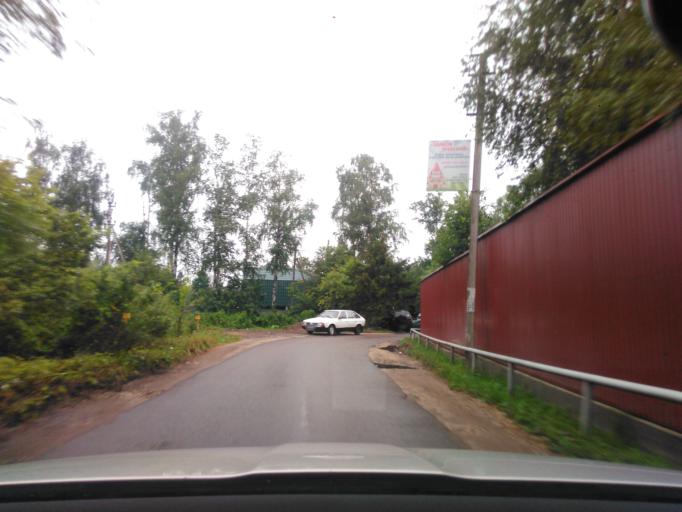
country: RU
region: Moskovskaya
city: Firsanovka
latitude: 55.9497
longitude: 37.2438
